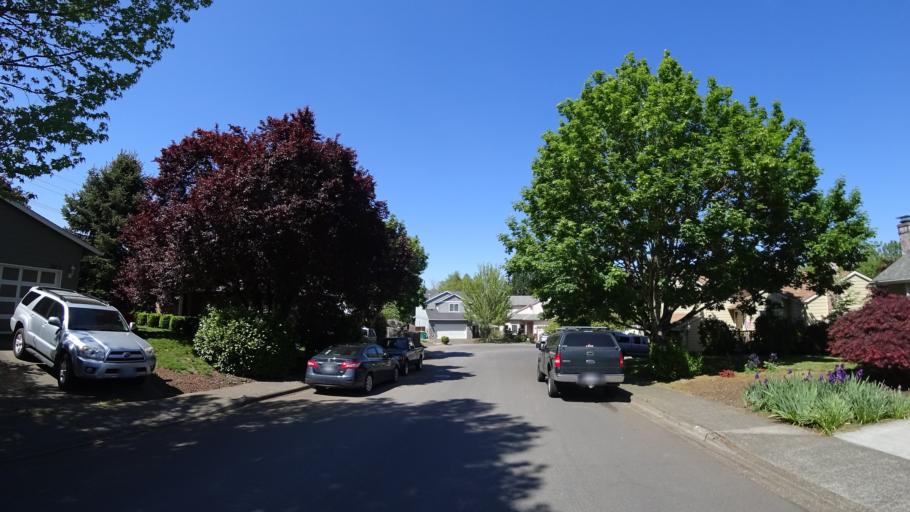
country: US
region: Oregon
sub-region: Washington County
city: Aloha
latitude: 45.4772
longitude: -122.8510
